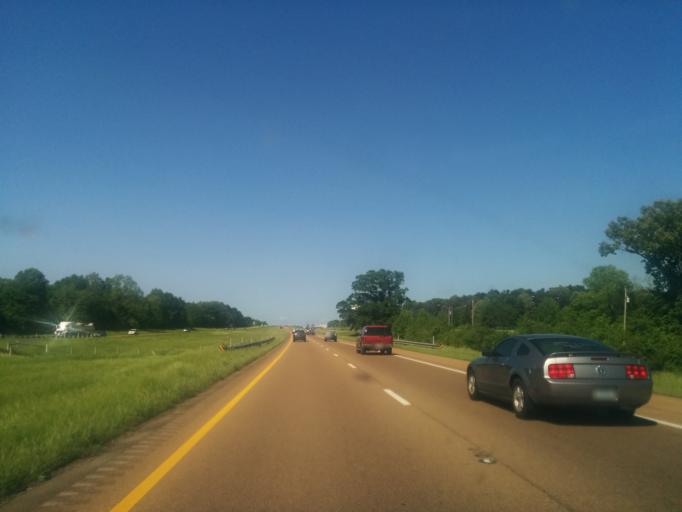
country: US
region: Mississippi
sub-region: Madison County
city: Canton
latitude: 32.5537
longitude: -90.0861
